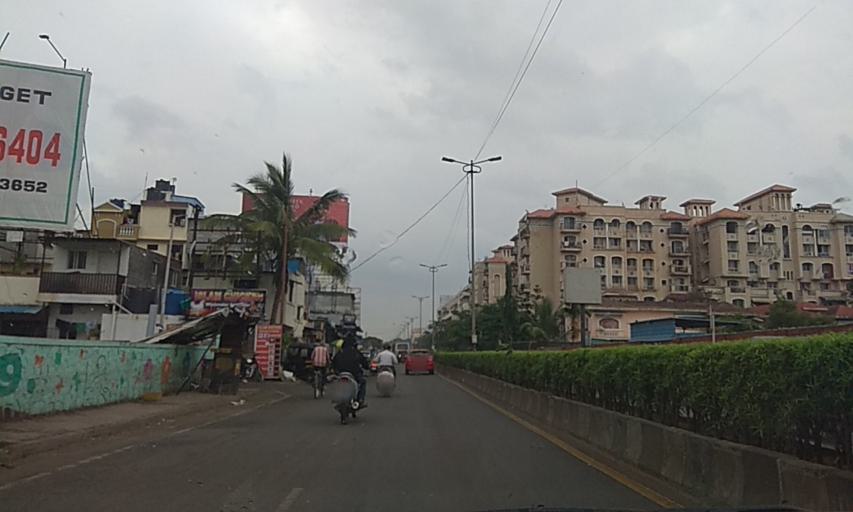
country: IN
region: Maharashtra
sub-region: Pune Division
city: Lohogaon
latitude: 18.5702
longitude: 73.9070
